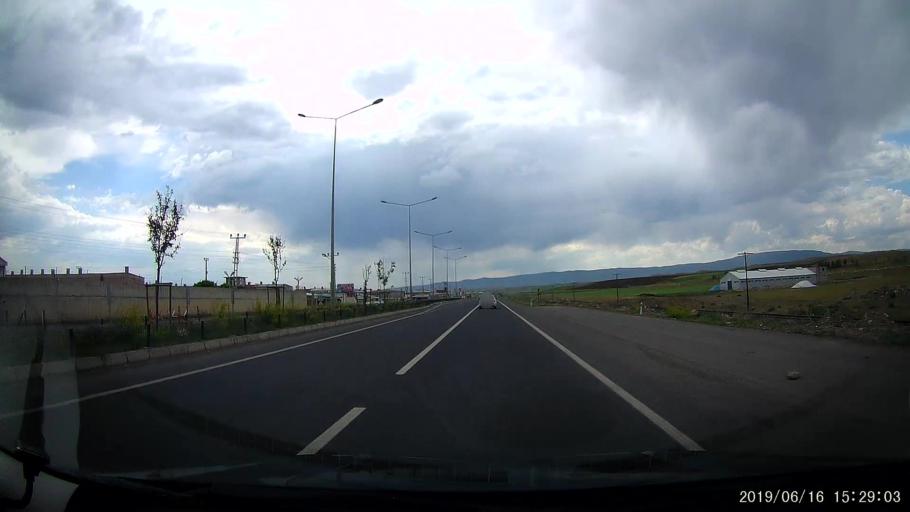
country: TR
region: Erzurum
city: Horasan
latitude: 40.0311
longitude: 42.1410
